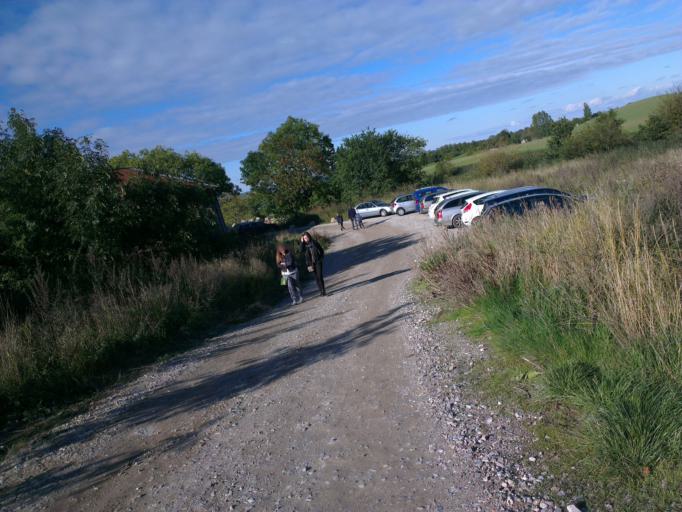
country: DK
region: Zealand
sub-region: Lejre Kommune
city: Ejby
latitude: 55.6802
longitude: 11.8439
